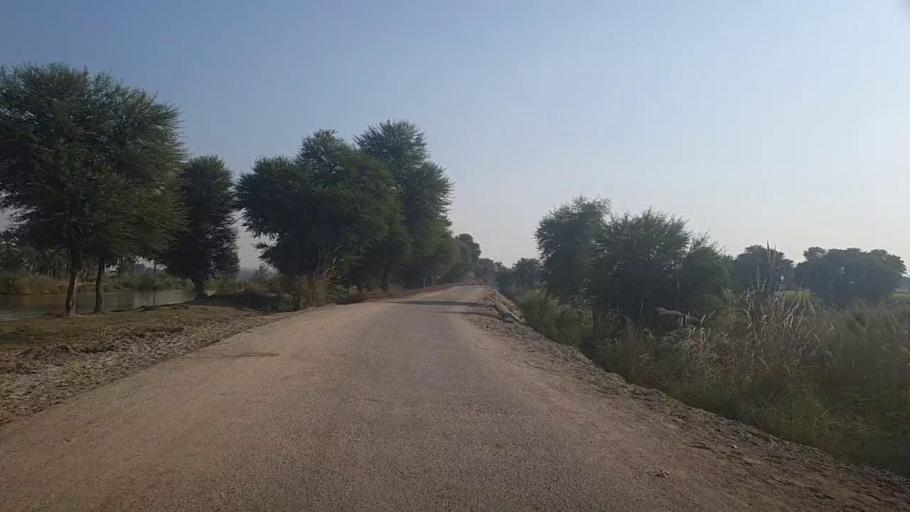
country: PK
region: Sindh
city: Kot Diji
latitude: 27.2666
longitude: 68.6744
